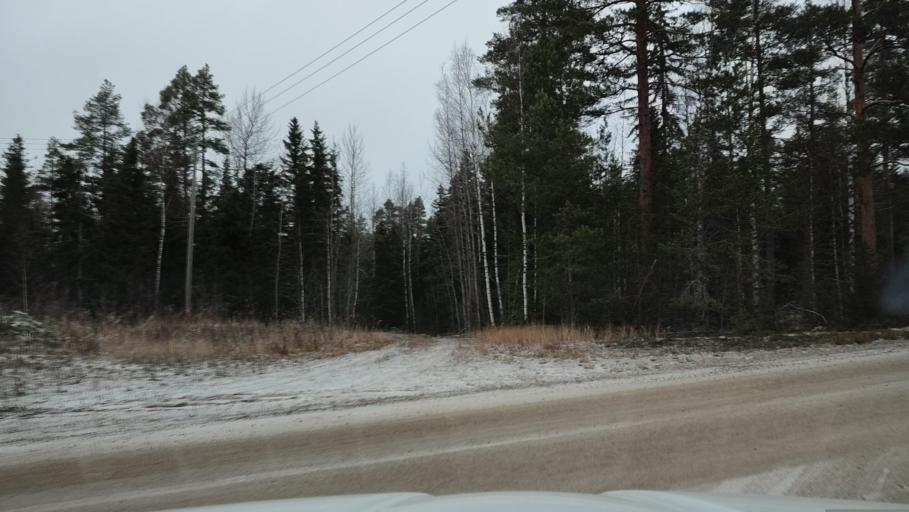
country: FI
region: Southern Ostrobothnia
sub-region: Suupohja
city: Karijoki
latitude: 62.2836
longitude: 21.6319
